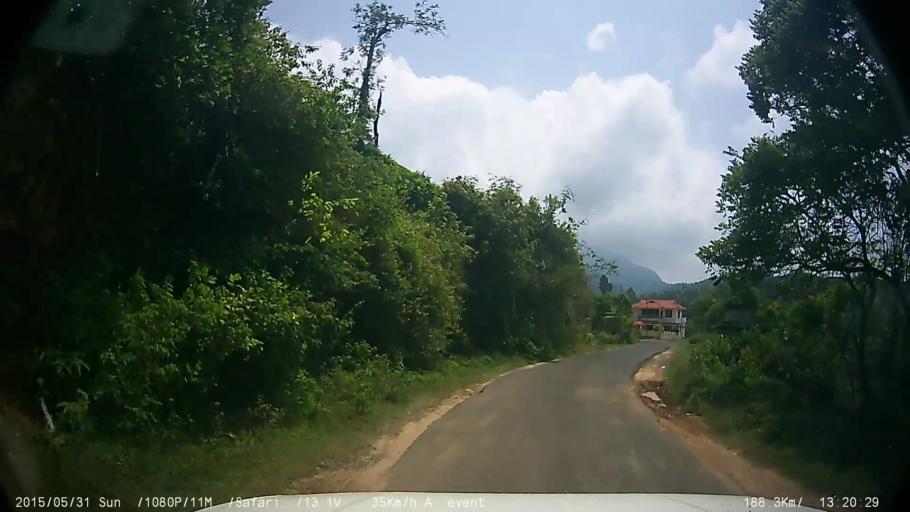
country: IN
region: Kerala
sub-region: Wayanad
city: Kalpetta
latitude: 11.5320
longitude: 76.1382
